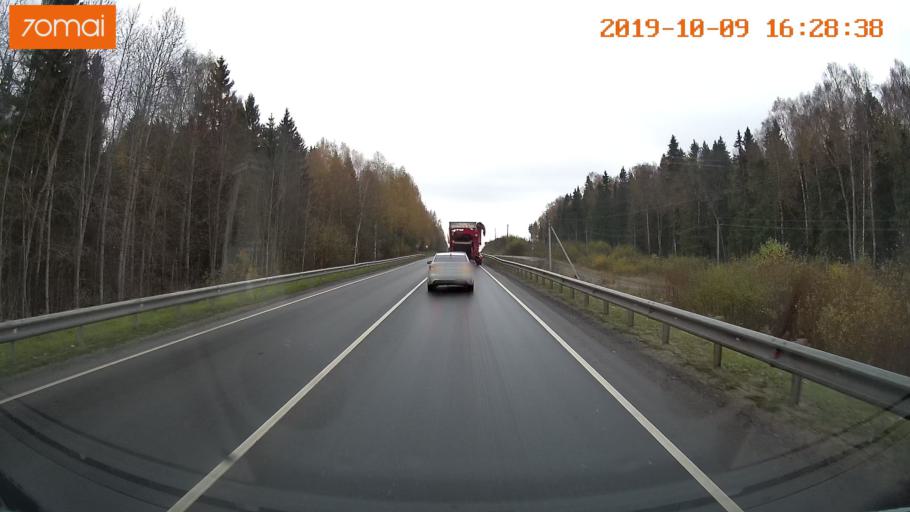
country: RU
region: Kostroma
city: Oktyabr'skiy
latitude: 57.6278
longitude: 40.9328
